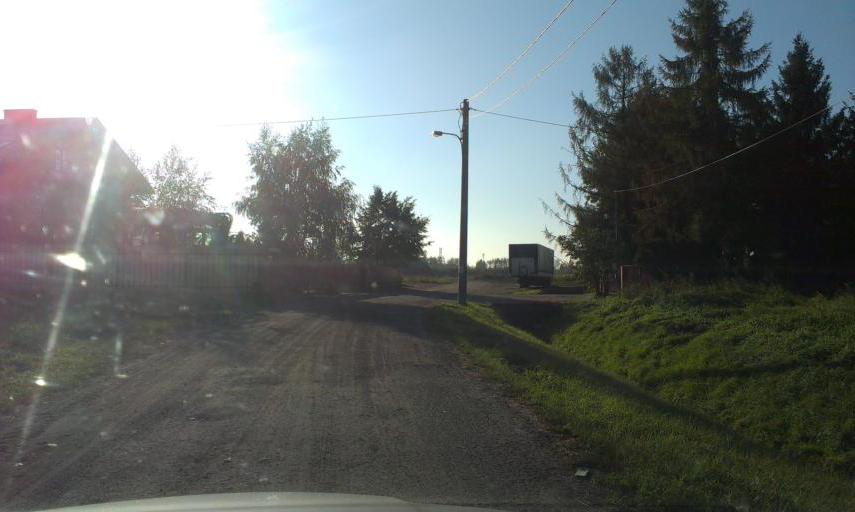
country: PL
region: Masovian Voivodeship
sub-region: Warszawa
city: Kabaty
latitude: 52.1157
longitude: 21.1024
